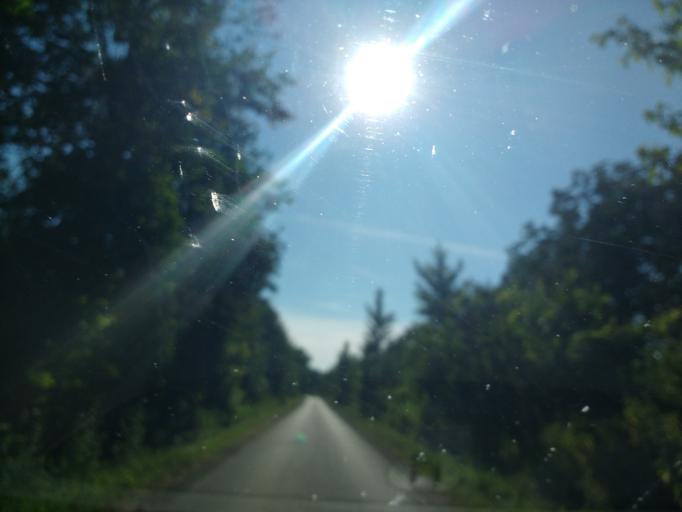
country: DE
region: North Rhine-Westphalia
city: Rietberg
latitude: 51.7209
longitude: 8.4223
